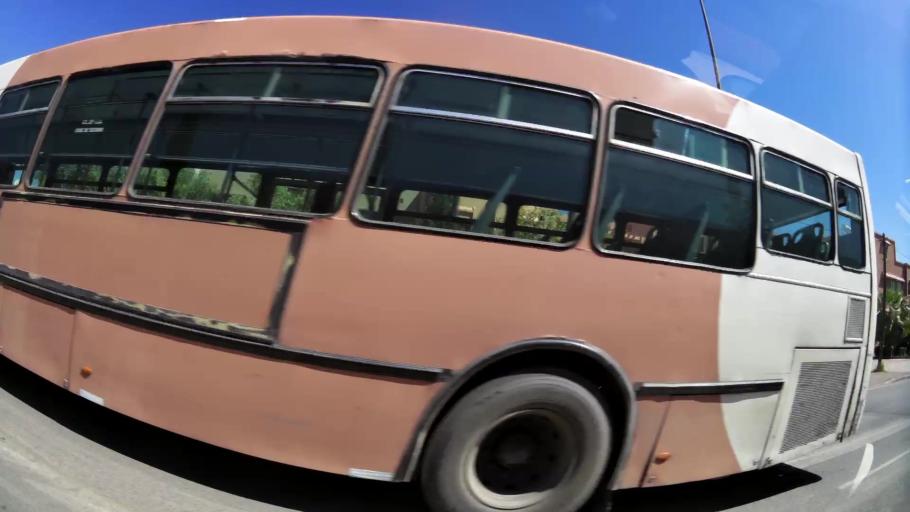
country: MA
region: Marrakech-Tensift-Al Haouz
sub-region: Marrakech
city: Marrakesh
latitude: 31.6386
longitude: -8.0636
